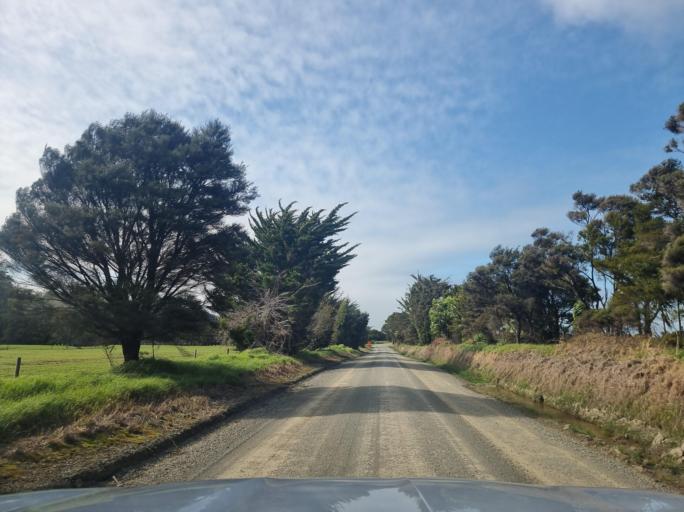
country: NZ
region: Auckland
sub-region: Auckland
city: Wellsford
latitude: -36.1050
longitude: 174.4995
